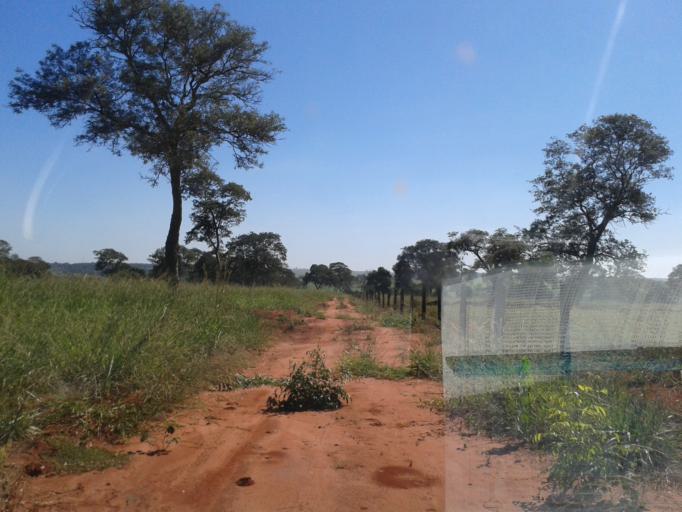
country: BR
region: Minas Gerais
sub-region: Santa Vitoria
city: Santa Vitoria
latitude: -19.0125
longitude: -50.3197
